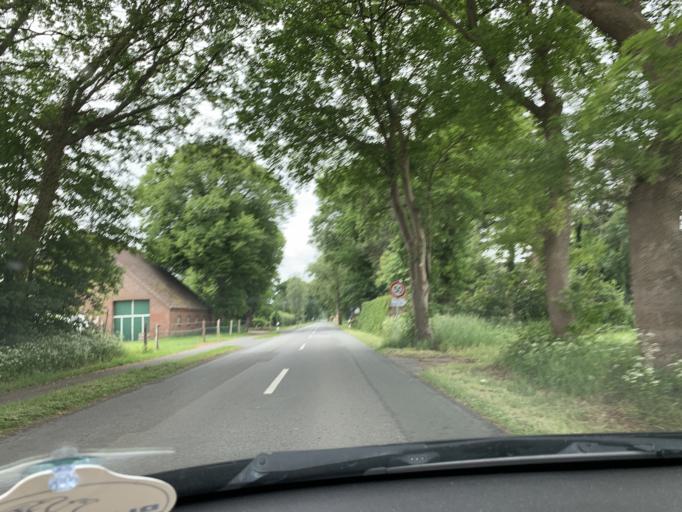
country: DE
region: Lower Saxony
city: Bockhorn
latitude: 53.3446
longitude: 8.0422
